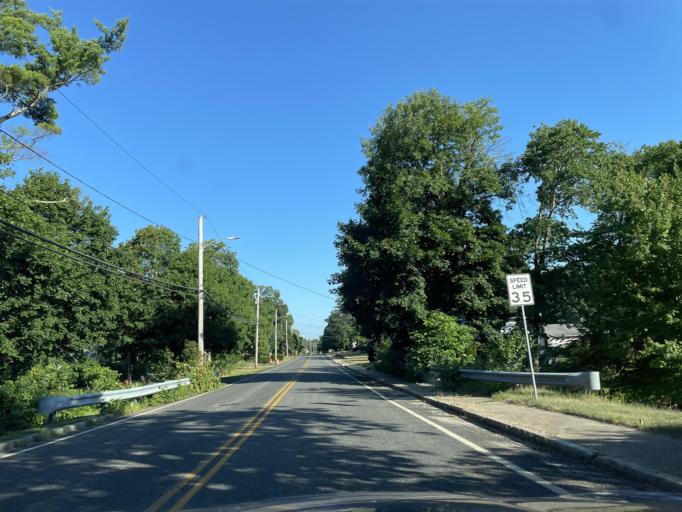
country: US
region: Massachusetts
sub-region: Bristol County
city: Mansfield
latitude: 42.0337
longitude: -71.2304
